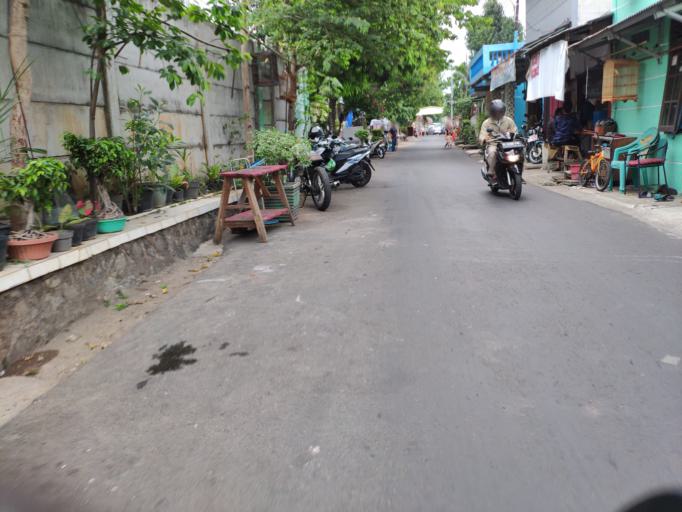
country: ID
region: Jakarta Raya
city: Jakarta
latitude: -6.2101
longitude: 106.8627
